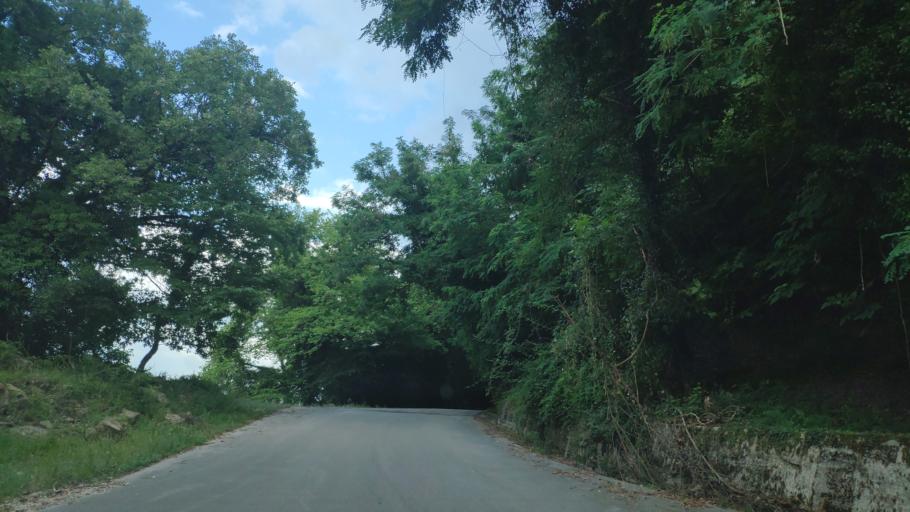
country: GR
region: Epirus
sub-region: Nomos Artas
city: Agios Dimitrios
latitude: 39.3896
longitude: 21.0197
